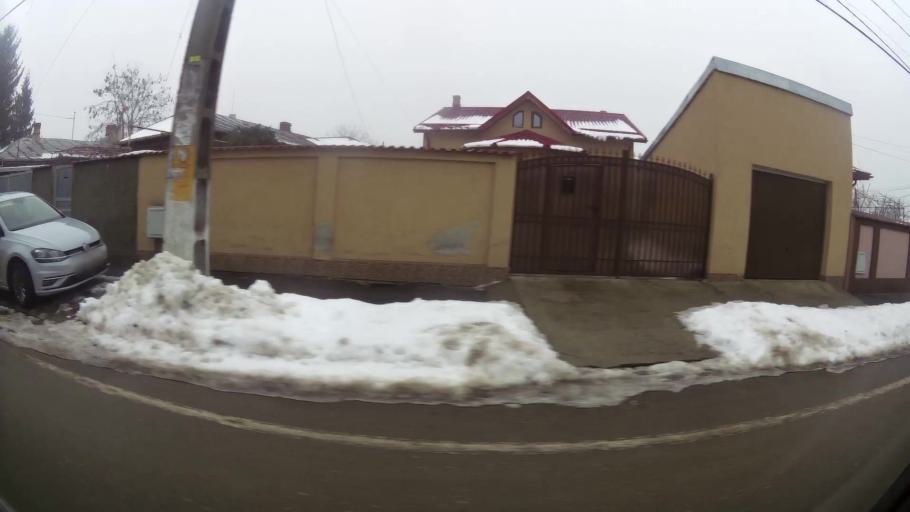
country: RO
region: Ilfov
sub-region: Comuna Chiajna
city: Chiajna
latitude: 44.4592
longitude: 25.9802
